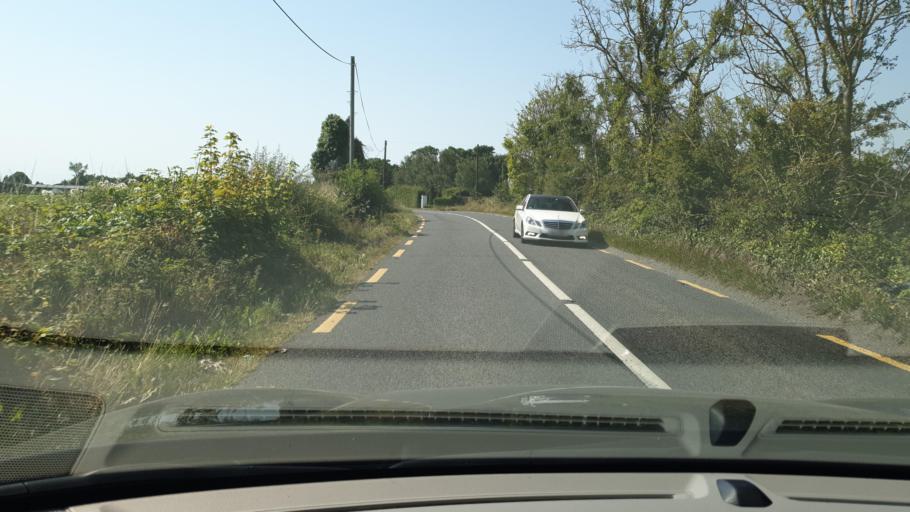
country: IE
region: Leinster
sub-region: An Mhi
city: Ratoath
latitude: 53.5168
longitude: -6.4936
